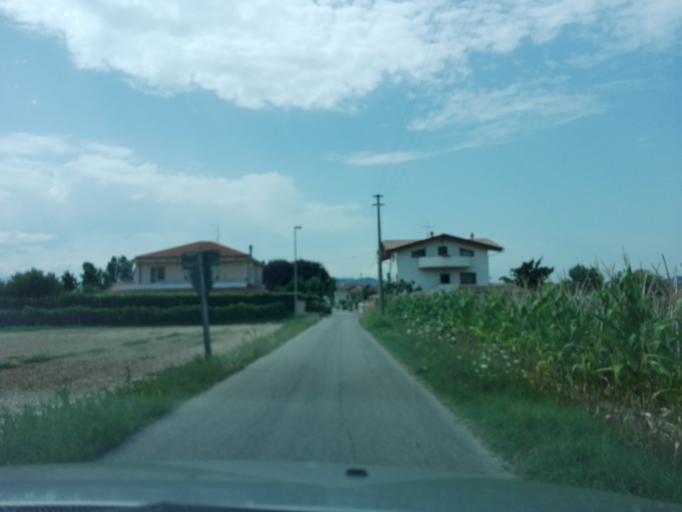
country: IT
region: Abruzzo
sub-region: Provincia di Pescara
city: Cappelle sul Tavo
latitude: 42.4898
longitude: 14.1201
